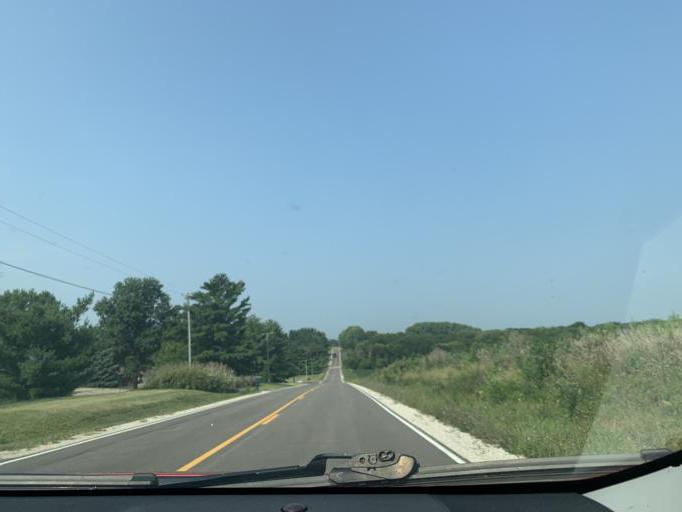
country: US
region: Illinois
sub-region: Whiteside County
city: Sterling
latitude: 41.8442
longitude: -89.7782
